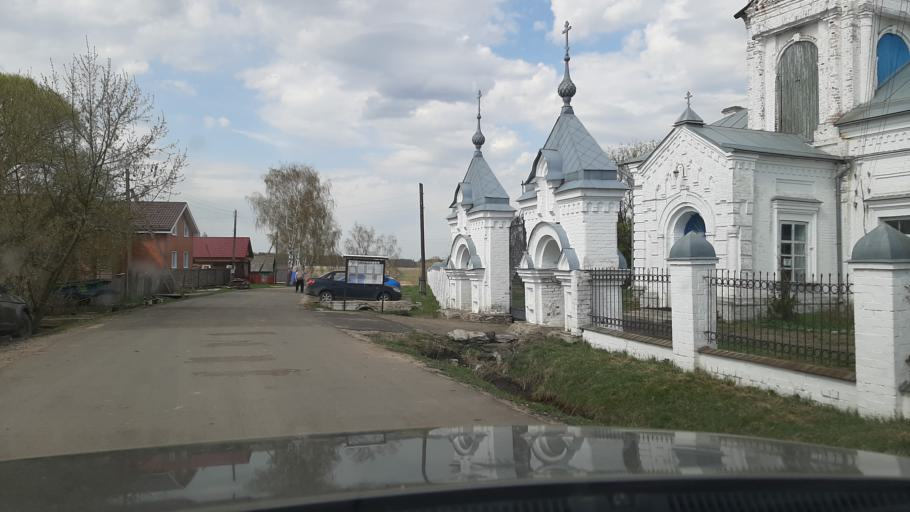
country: RU
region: Ivanovo
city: Privolzhsk
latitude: 57.3324
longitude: 41.2326
